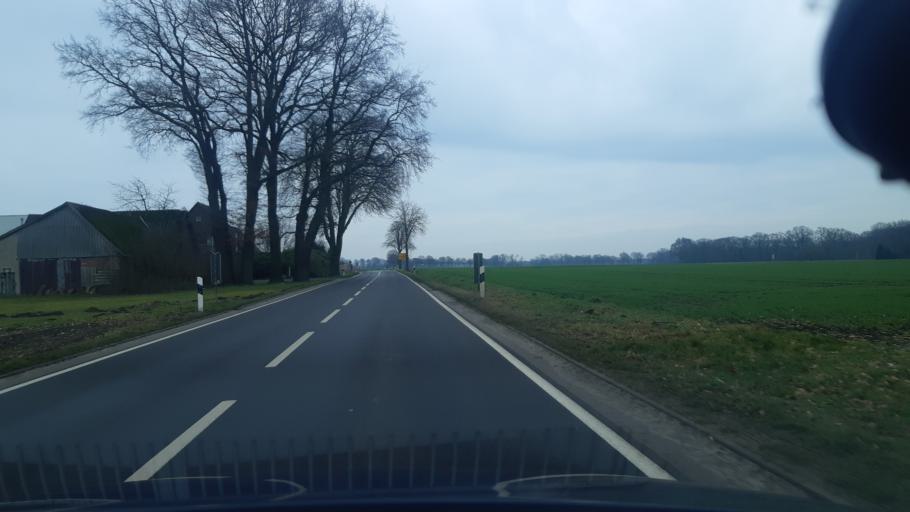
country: DE
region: Lower Saxony
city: Cloppenburg
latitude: 52.8121
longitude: 8.0254
